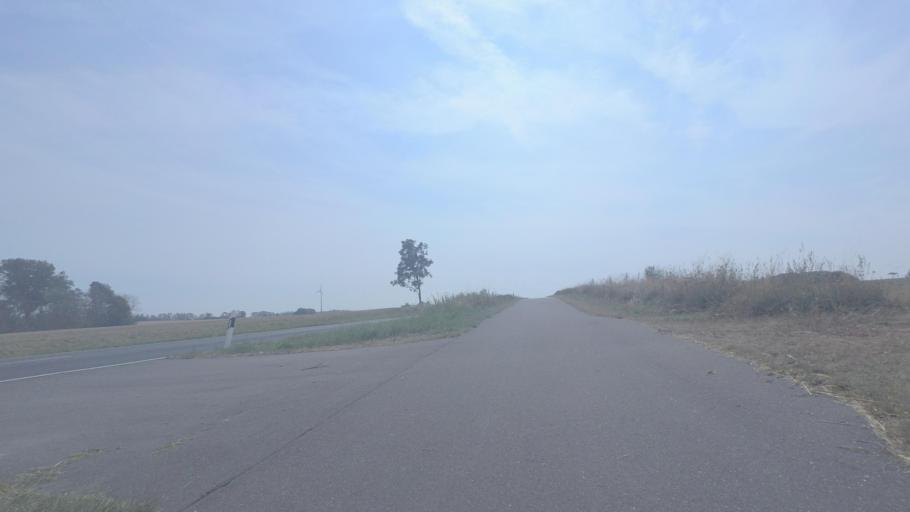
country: DE
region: Mecklenburg-Vorpommern
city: Garz
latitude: 54.3027
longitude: 13.3510
